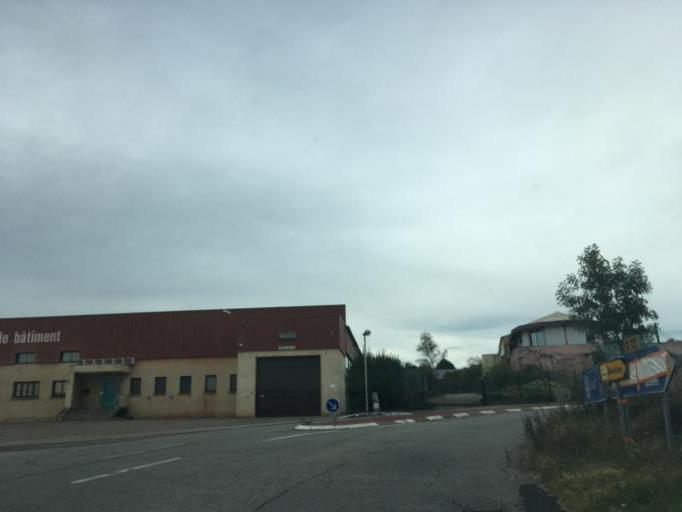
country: FR
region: Rhone-Alpes
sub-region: Departement de la Loire
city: Saint-Martin-la-Plaine
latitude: 45.5401
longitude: 4.5932
